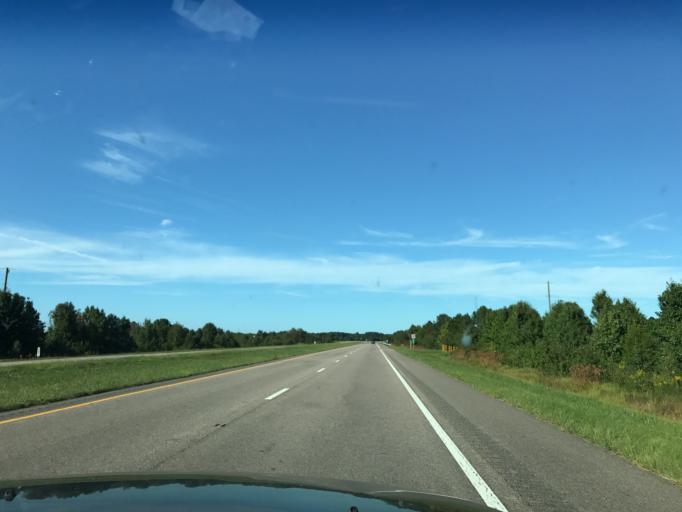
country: US
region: Virginia
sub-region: City of Portsmouth
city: Portsmouth Heights
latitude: 36.6955
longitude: -76.3452
